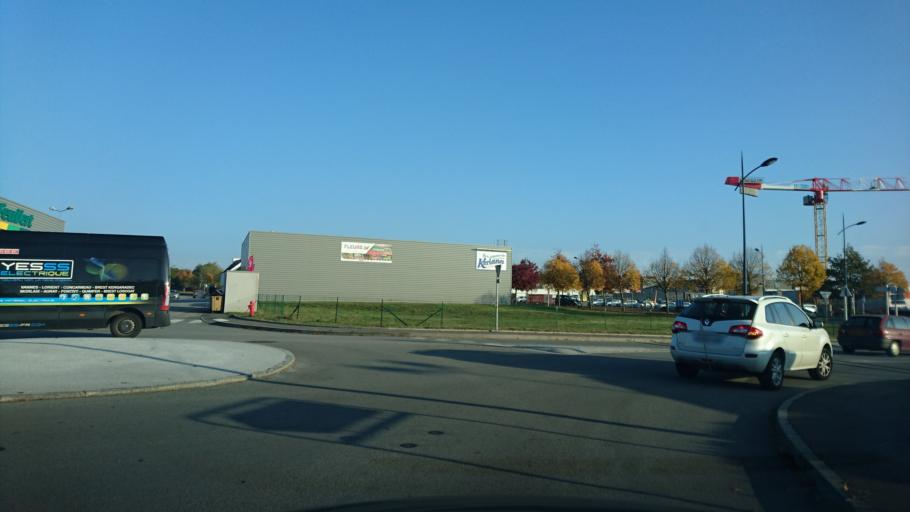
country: FR
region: Brittany
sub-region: Departement du Morbihan
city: Auray
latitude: 47.6645
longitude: -3.0062
